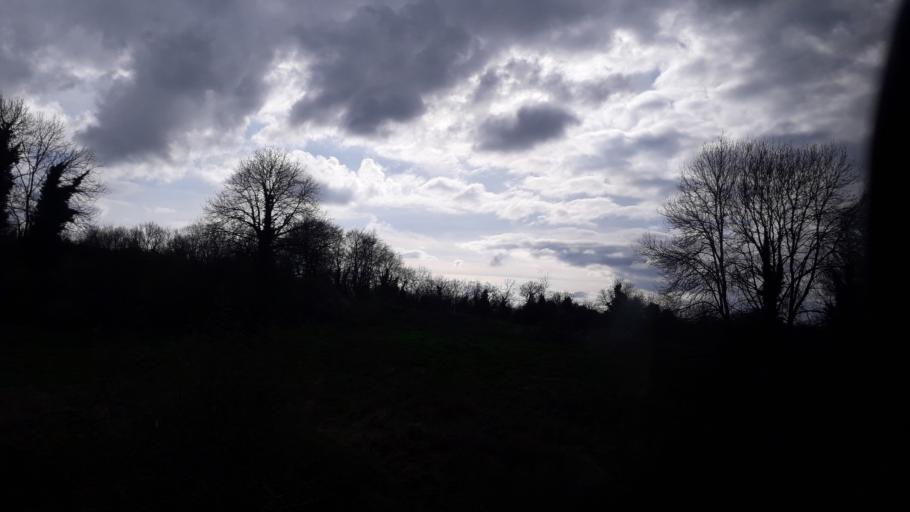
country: IE
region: Leinster
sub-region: An Iarmhi
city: Rochfortbridge
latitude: 53.4971
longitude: -7.2425
